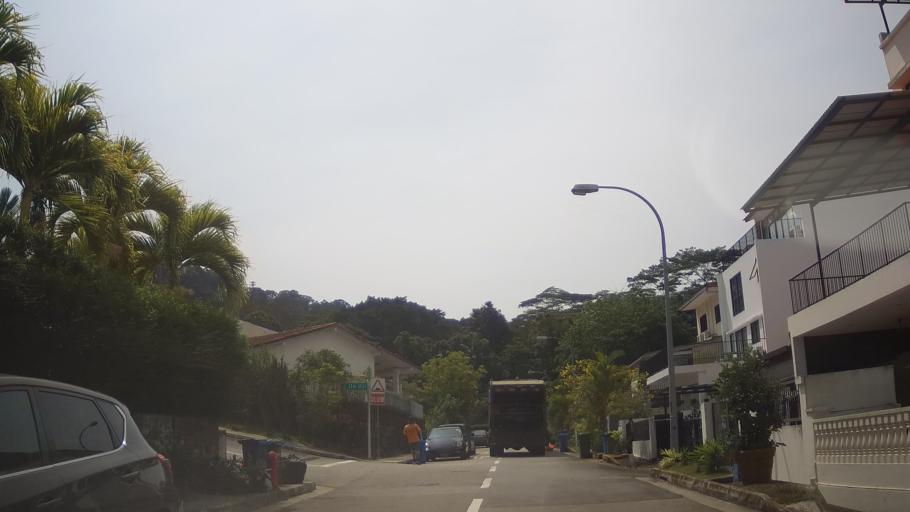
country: SG
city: Singapore
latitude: 1.3584
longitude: 103.7686
